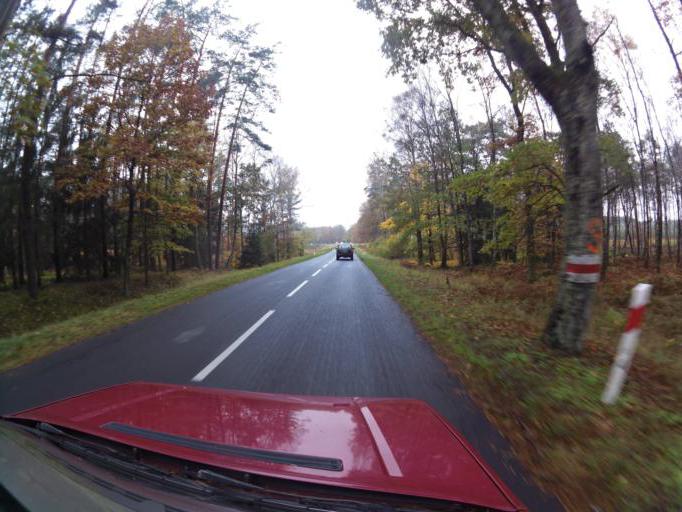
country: PL
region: West Pomeranian Voivodeship
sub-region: Powiat policki
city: Dobra
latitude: 53.5782
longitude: 14.4271
